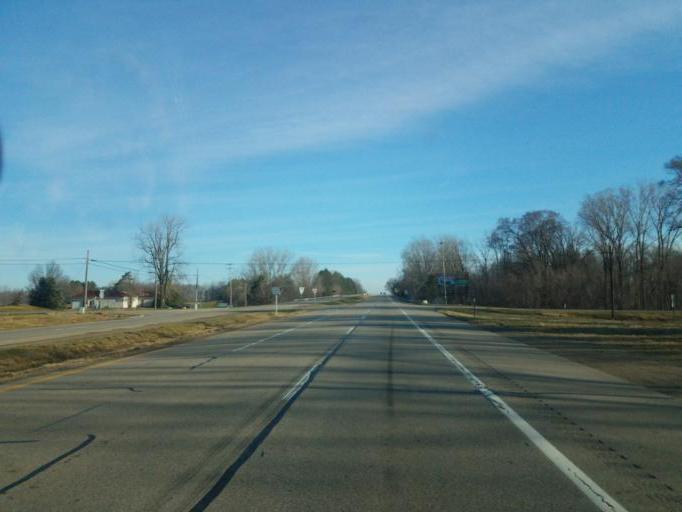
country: US
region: Michigan
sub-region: Clinton County
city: Saint Johns
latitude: 43.1031
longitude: -84.5633
